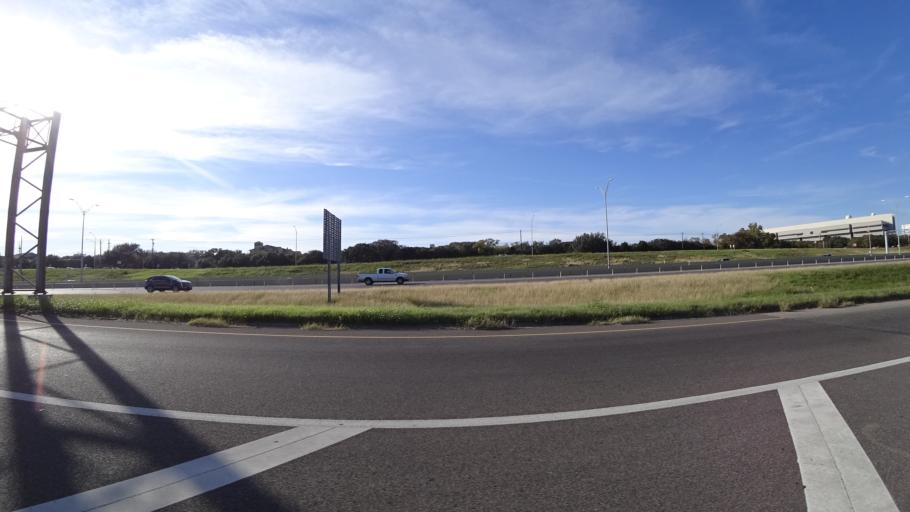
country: US
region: Texas
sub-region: Williamson County
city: Jollyville
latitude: 30.3910
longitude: -97.7334
